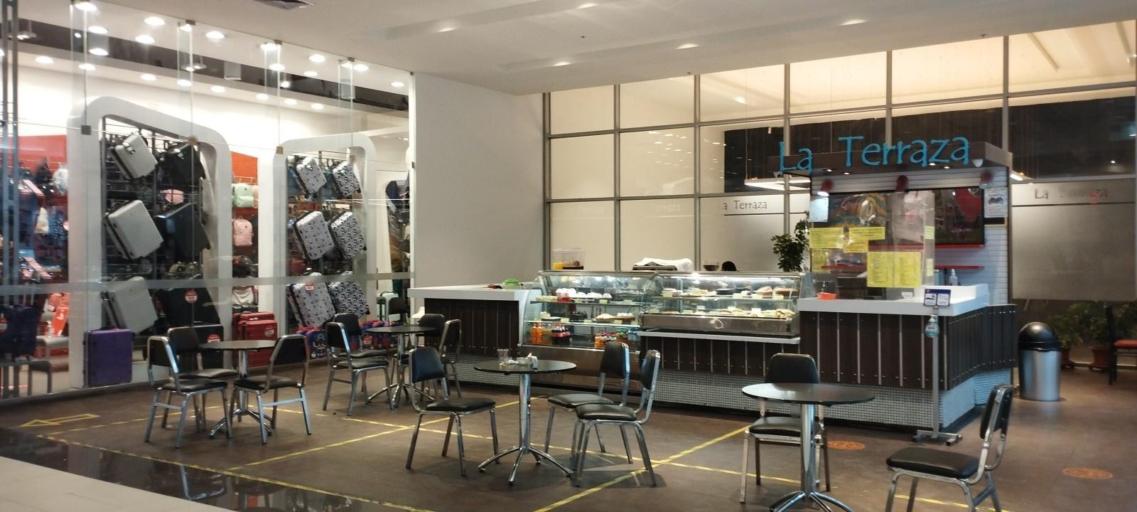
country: PE
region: Cusco
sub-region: Provincia de Cusco
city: Cusco
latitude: -13.5229
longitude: -71.9502
